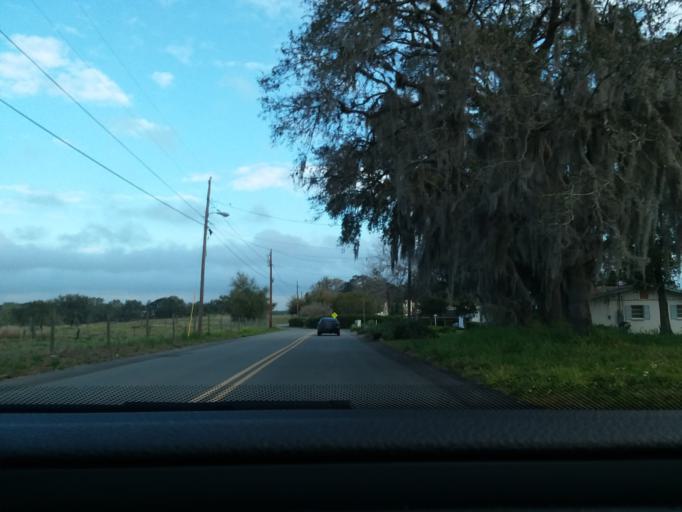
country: US
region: Florida
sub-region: Polk County
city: Haines City
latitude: 28.1187
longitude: -81.6526
